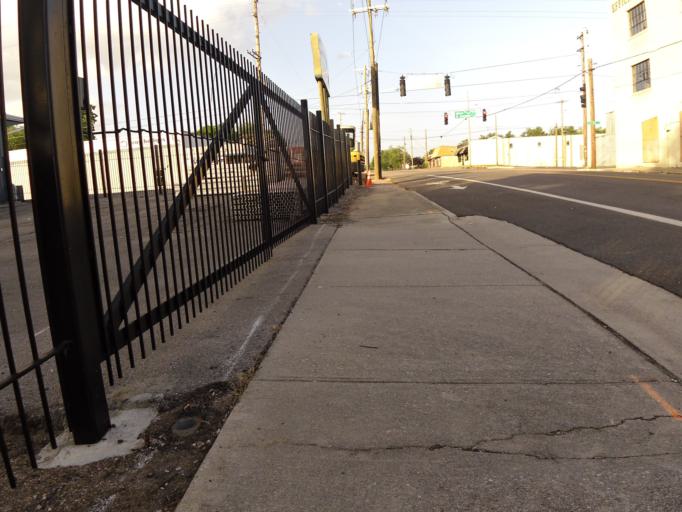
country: US
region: Tennessee
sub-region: Knox County
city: Knoxville
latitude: 35.9749
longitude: -83.9114
